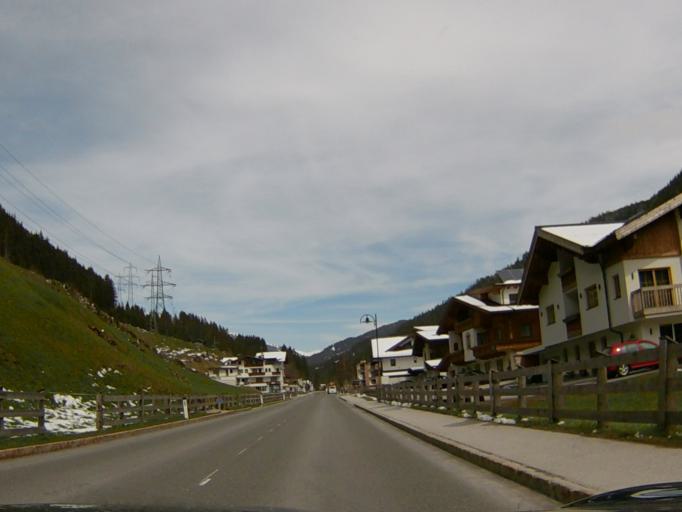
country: AT
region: Tyrol
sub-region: Politischer Bezirk Schwaz
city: Gerlos
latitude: 47.2151
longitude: 12.0104
